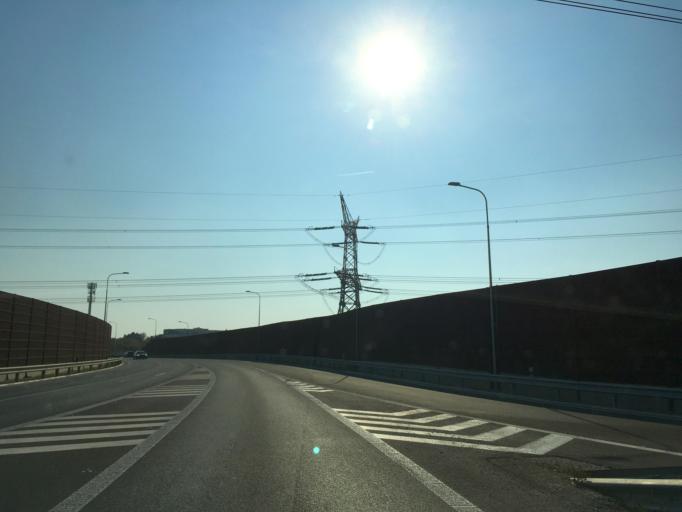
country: SK
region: Bratislavsky
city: Dunajska Luzna
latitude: 48.1083
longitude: 17.2253
